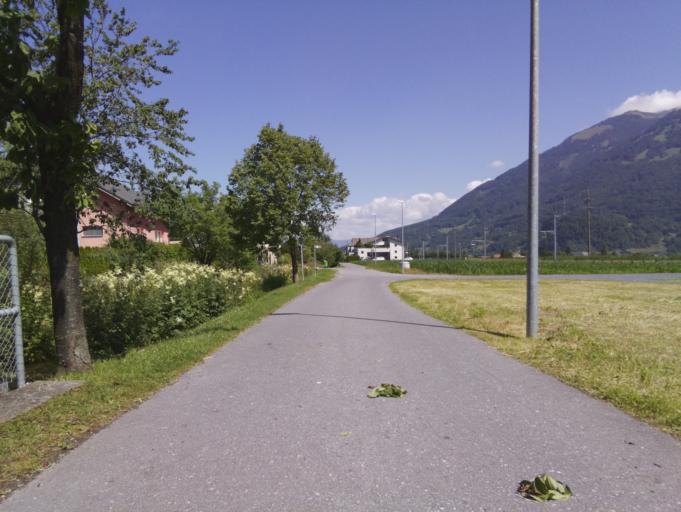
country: CH
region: Glarus
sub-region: Glarus
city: Oberurnen
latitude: 47.1132
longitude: 9.0653
